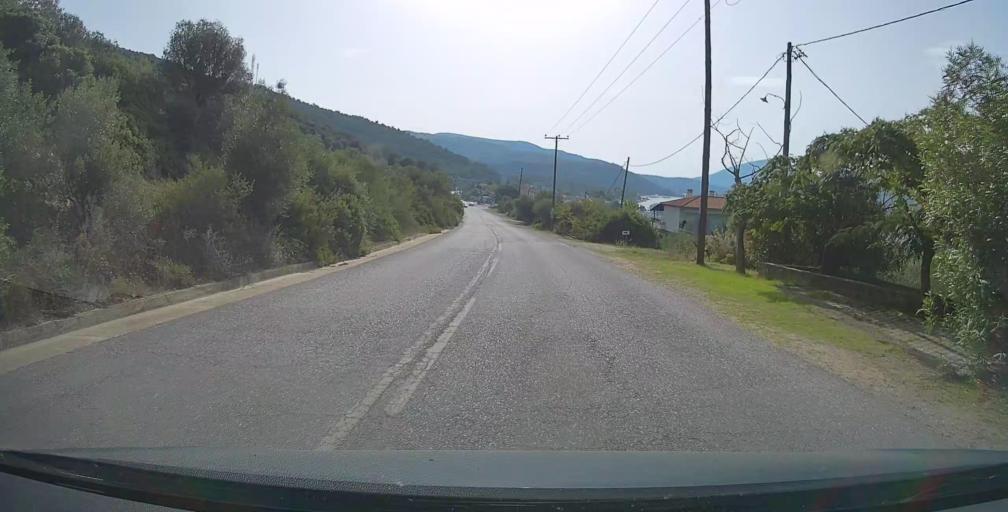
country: GR
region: Central Macedonia
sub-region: Nomos Chalkidikis
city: Sykia
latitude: 39.9738
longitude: 23.9129
